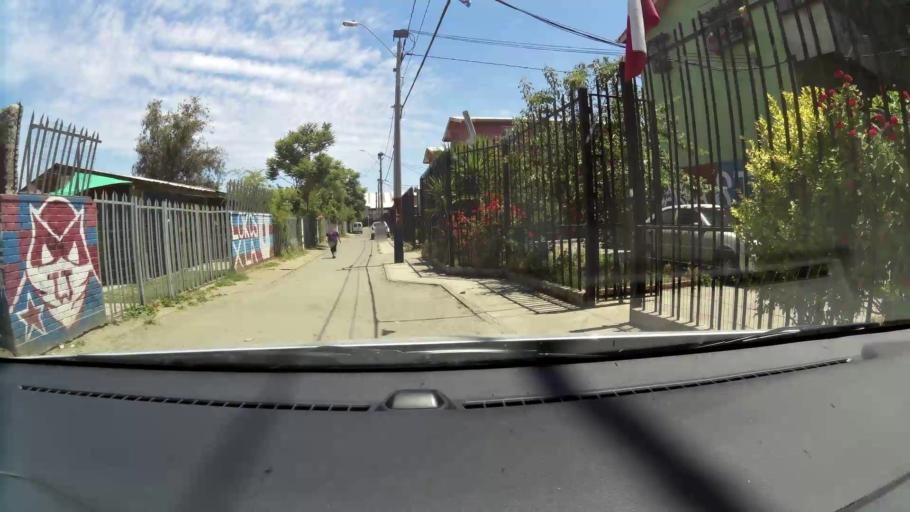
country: CL
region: Santiago Metropolitan
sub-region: Provincia de Santiago
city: La Pintana
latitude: -33.5582
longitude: -70.6201
